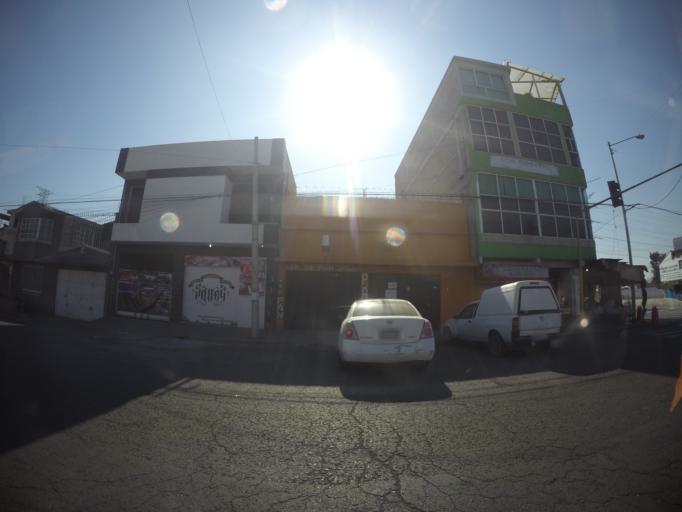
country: MX
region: Mexico
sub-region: Atenco
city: Colonia el Salado
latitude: 19.5901
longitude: -99.0273
